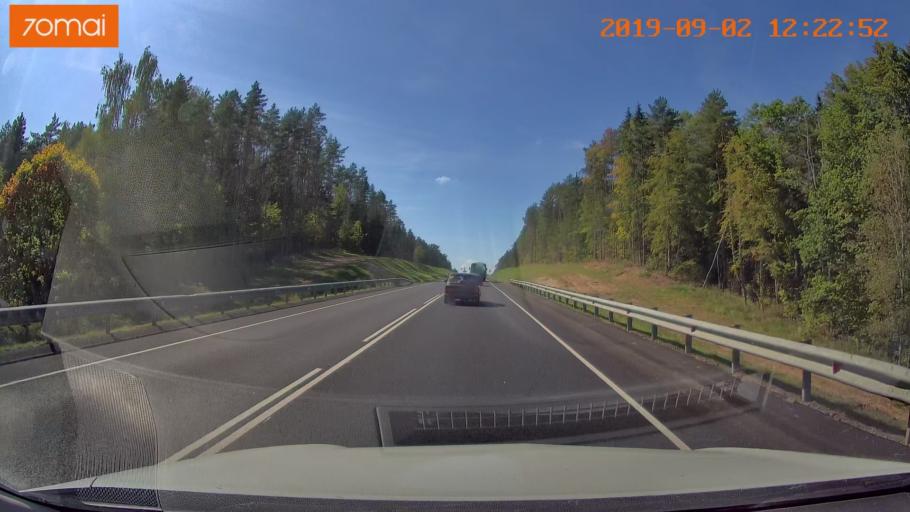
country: RU
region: Smolensk
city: Shumyachi
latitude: 53.8782
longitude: 32.6274
